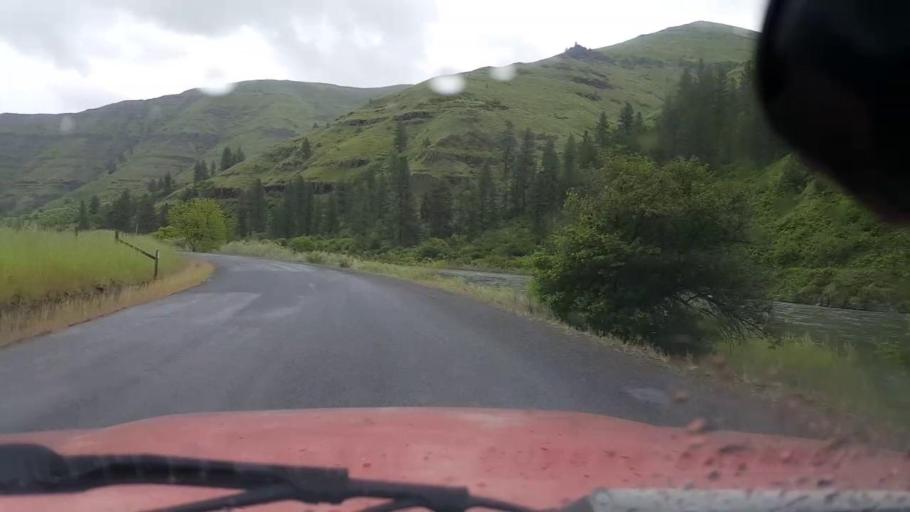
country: US
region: Washington
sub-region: Asotin County
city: Asotin
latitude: 46.0277
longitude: -117.3123
